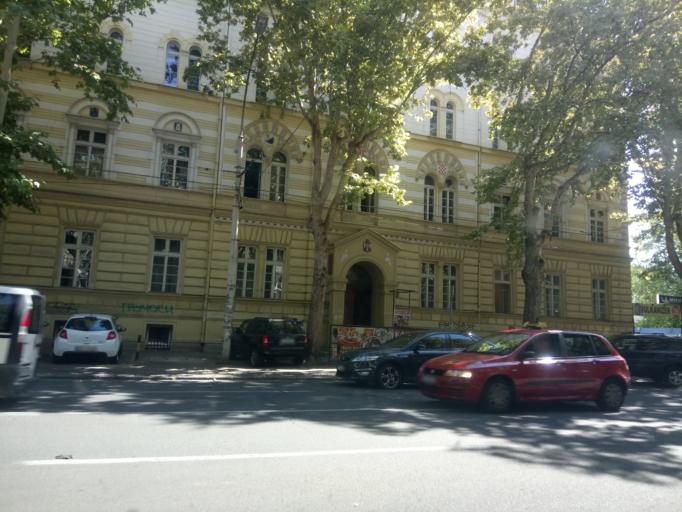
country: RS
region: Central Serbia
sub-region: Belgrade
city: Stari Grad
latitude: 44.8245
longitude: 20.4578
